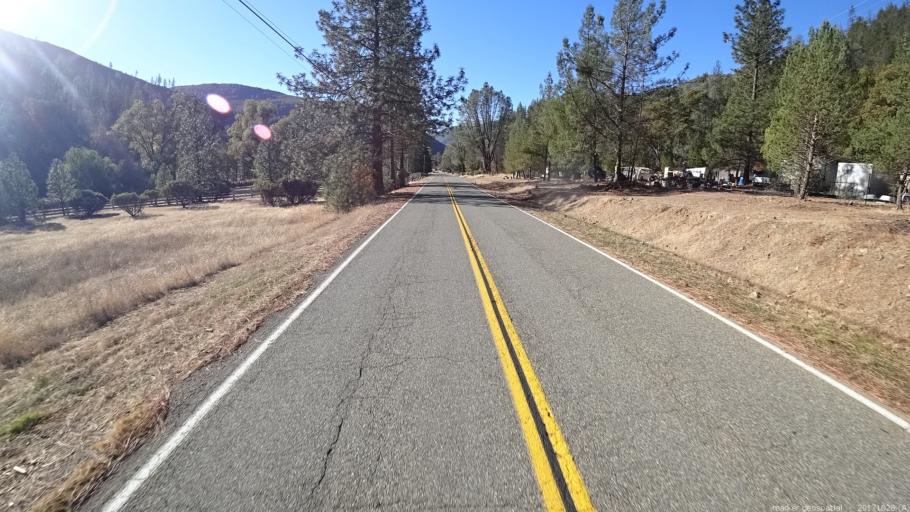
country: US
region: California
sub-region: Trinity County
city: Lewiston
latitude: 40.7238
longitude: -122.6268
